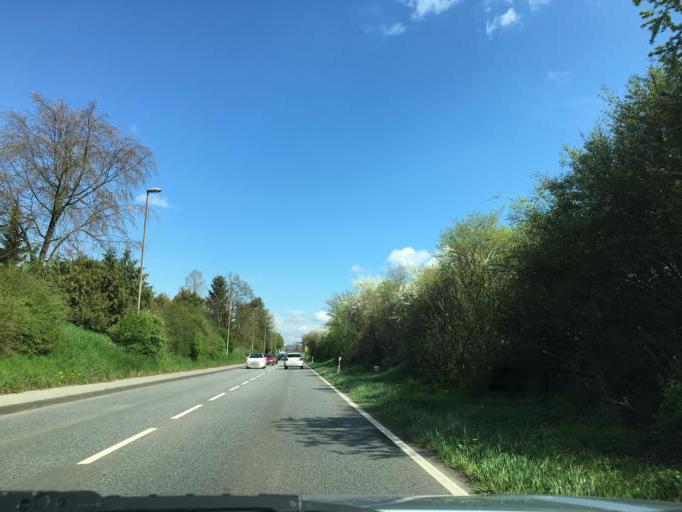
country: DE
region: Hesse
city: Heusenstamm
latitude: 50.0541
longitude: 8.8073
